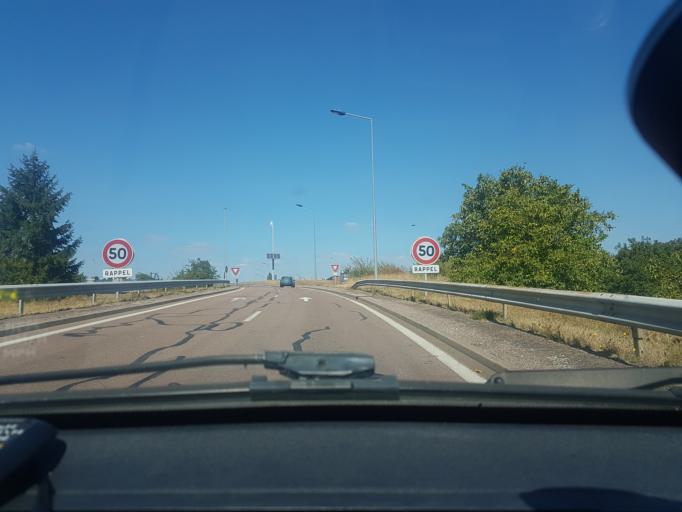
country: FR
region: Bourgogne
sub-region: Departement de la Cote-d'Or
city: Saint-Apollinaire
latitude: 47.3249
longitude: 5.0788
